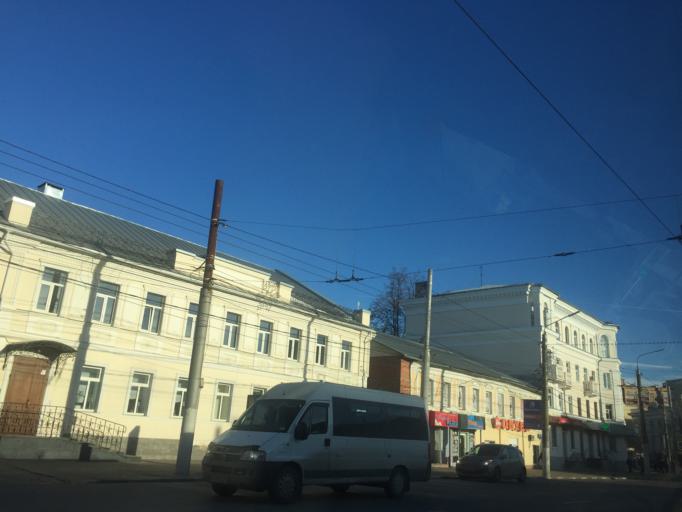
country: RU
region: Tula
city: Tula
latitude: 54.1903
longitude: 37.6214
